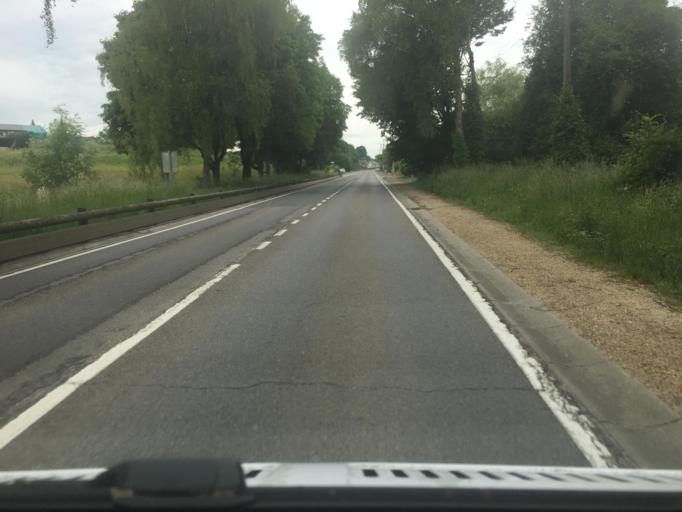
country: BE
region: Wallonia
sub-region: Province du Luxembourg
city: Florenville
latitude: 49.7025
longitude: 5.3273
